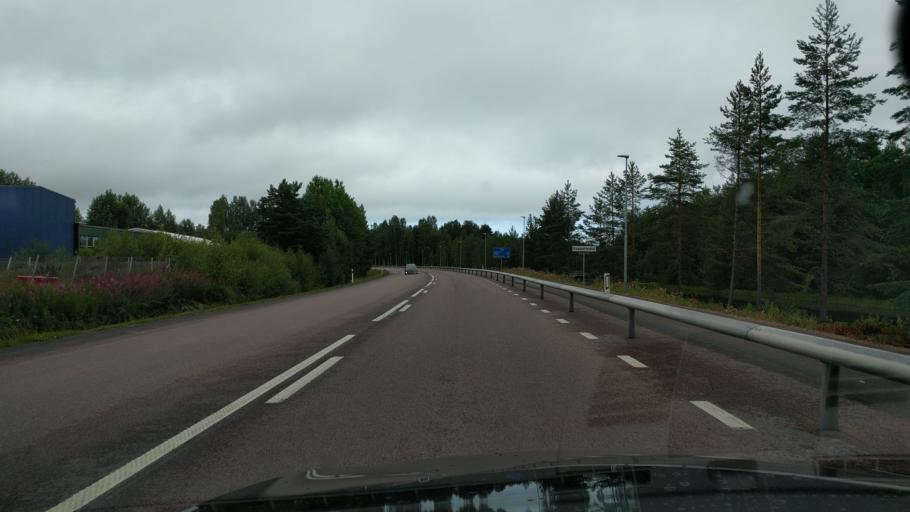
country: SE
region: Dalarna
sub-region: Mora Kommun
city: Mora
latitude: 61.0183
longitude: 14.5387
